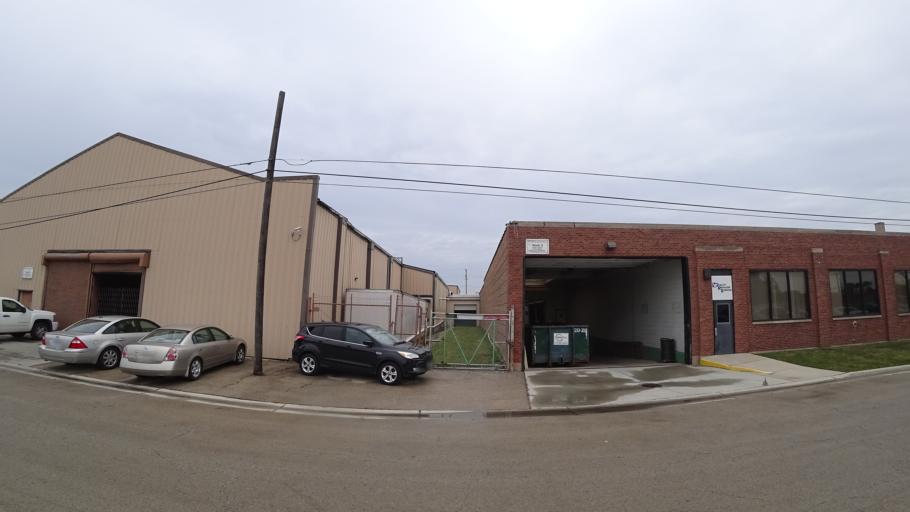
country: US
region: Illinois
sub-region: Cook County
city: Cicero
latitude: 41.8599
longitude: -87.7629
